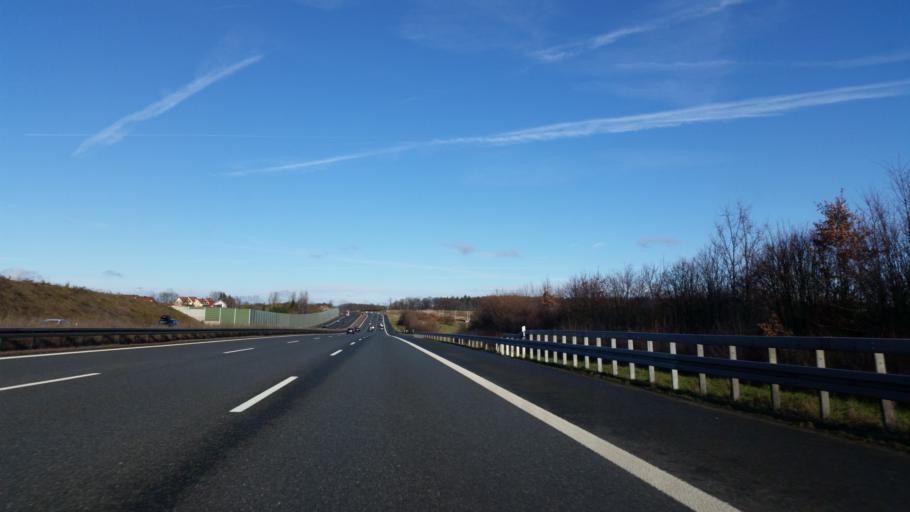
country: DE
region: Bavaria
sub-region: Upper Bavaria
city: Stammham
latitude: 48.8674
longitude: 11.4672
